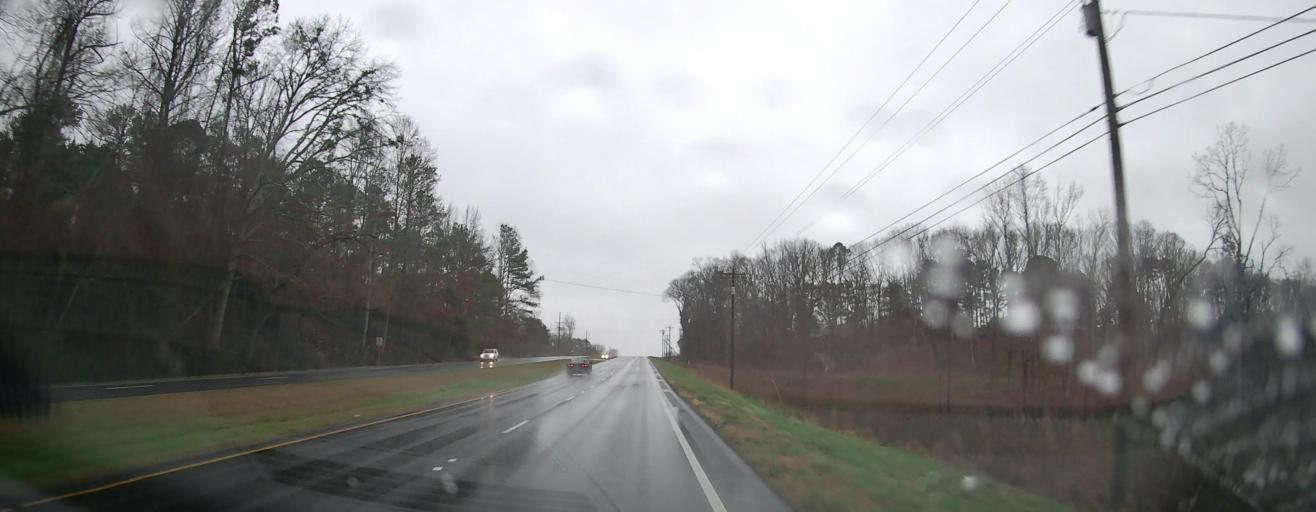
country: US
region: Alabama
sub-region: Morgan County
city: Flint City
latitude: 34.4828
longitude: -86.9631
